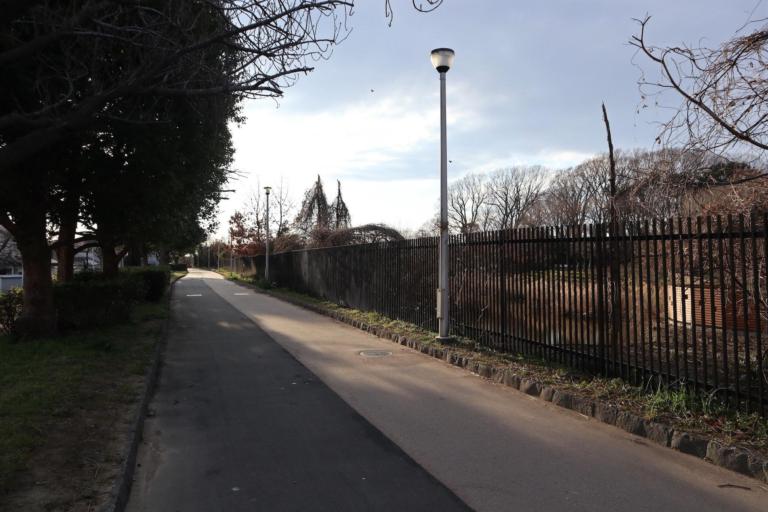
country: JP
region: Saitama
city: Yashio-shi
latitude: 35.7940
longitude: 139.8615
